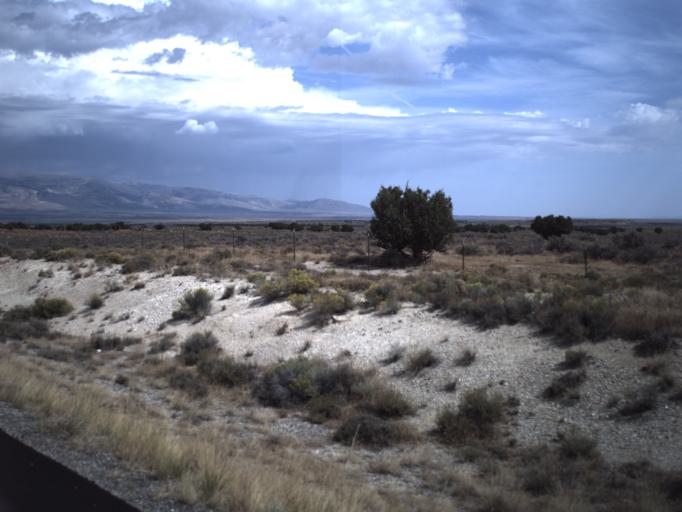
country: US
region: Idaho
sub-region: Cassia County
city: Burley
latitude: 41.7101
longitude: -113.5303
